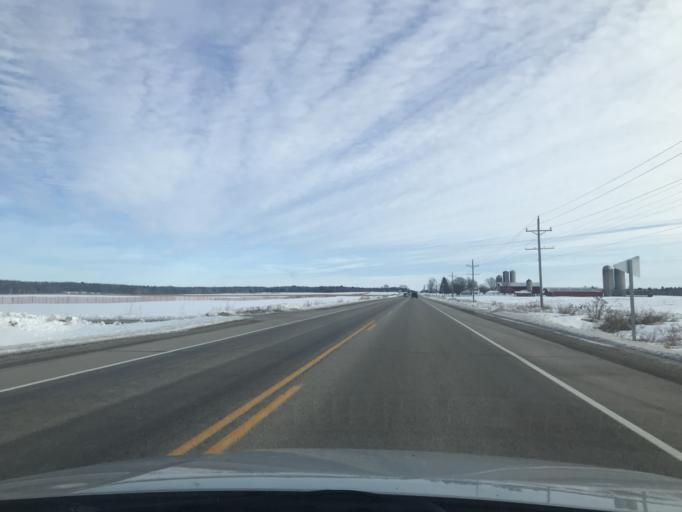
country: US
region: Wisconsin
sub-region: Oconto County
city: Gillett
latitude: 44.8959
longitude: -88.2345
